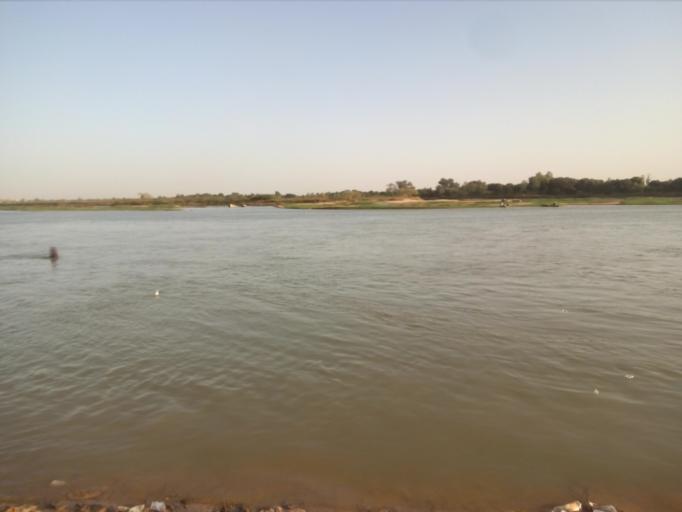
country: NE
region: Niamey
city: Niamey
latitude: 13.5204
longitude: 2.0732
